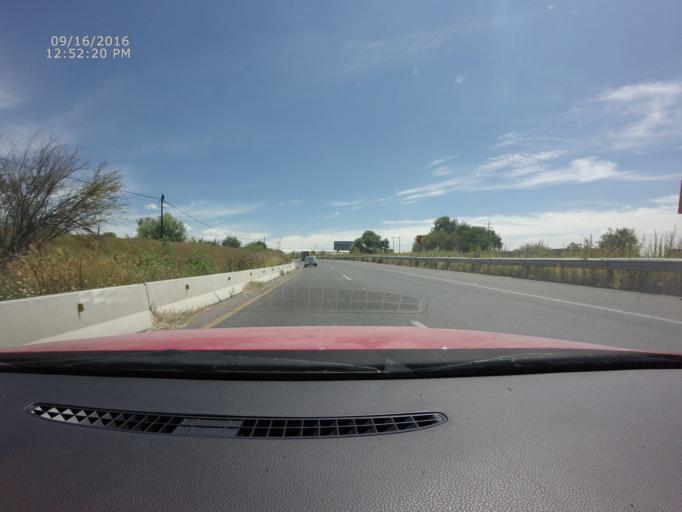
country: MX
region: Queretaro
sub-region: Colon
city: Purisima de Cubos (La Purisima)
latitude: 20.6158
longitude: -100.1434
